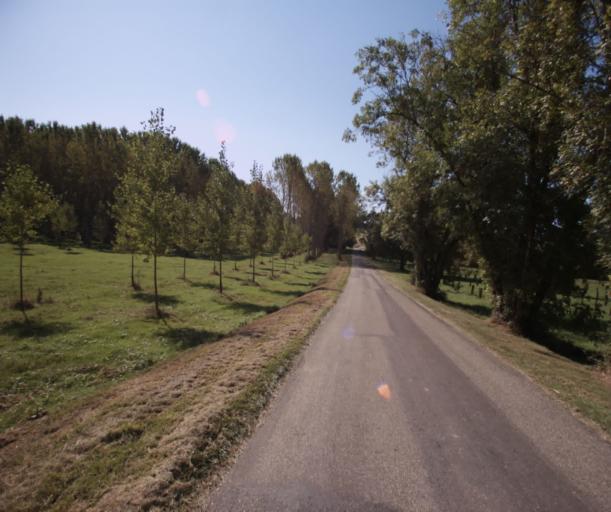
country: FR
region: Midi-Pyrenees
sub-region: Departement du Gers
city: Cazaubon
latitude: 43.9325
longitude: -0.0220
